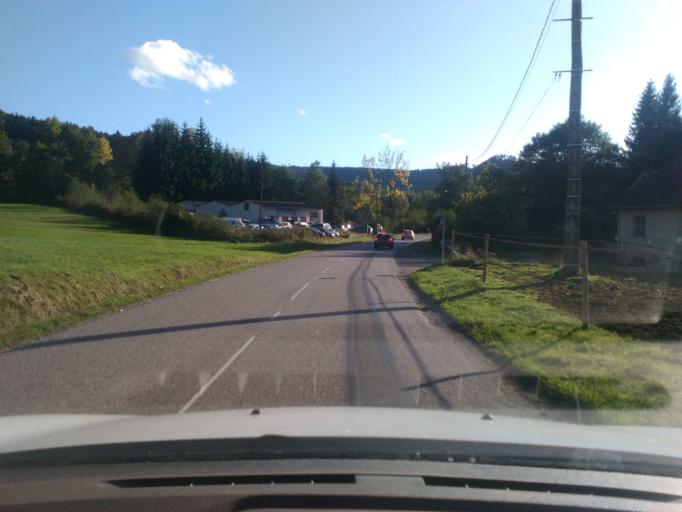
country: FR
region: Lorraine
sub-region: Departement des Vosges
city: Saint-Michel-sur-Meurthe
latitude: 48.3160
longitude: 6.8417
